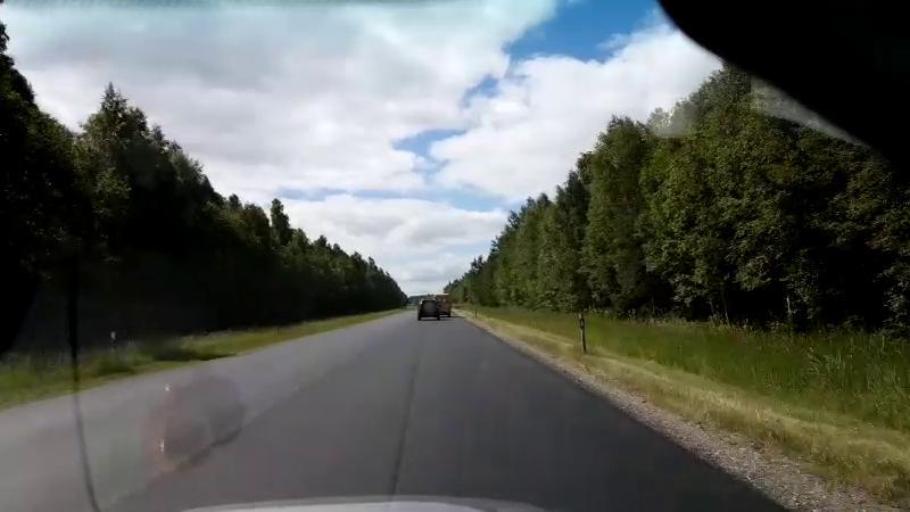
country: LV
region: Salacgrivas
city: Ainazi
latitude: 57.9733
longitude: 24.4528
